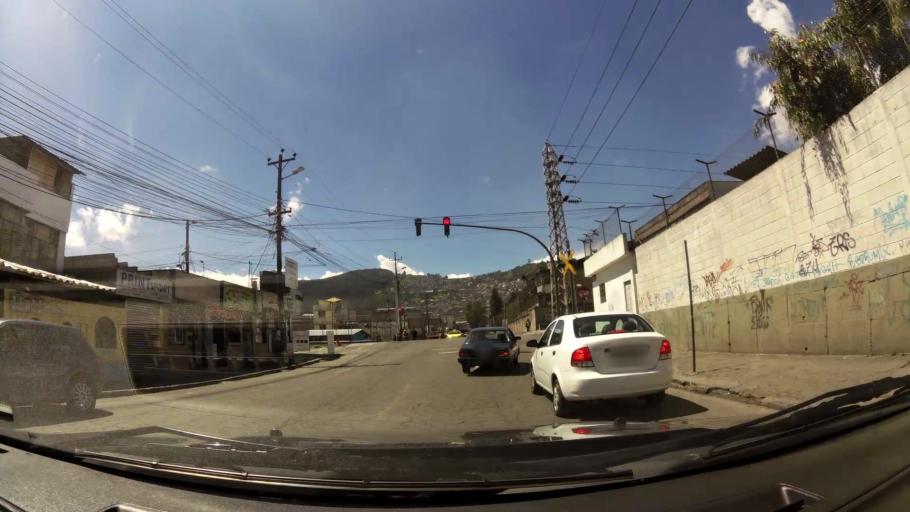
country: EC
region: Pichincha
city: Quito
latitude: -0.2688
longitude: -78.5311
